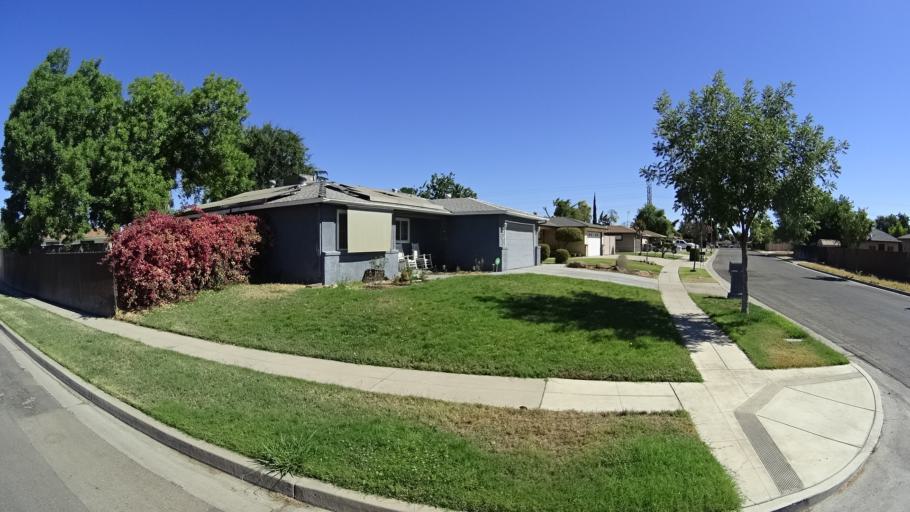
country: US
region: California
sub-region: Fresno County
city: Fresno
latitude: 36.7981
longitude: -119.8398
